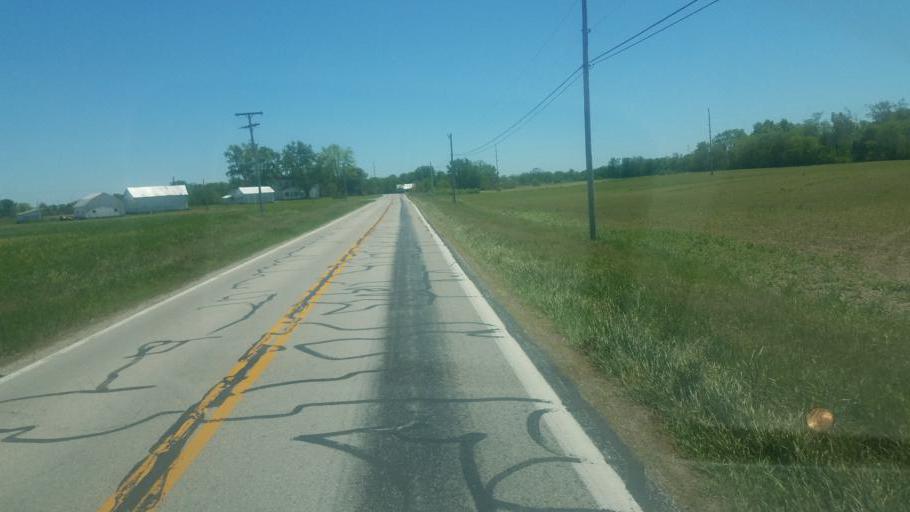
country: US
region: Ohio
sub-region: Darke County
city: Versailles
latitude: 40.2351
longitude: -84.5053
